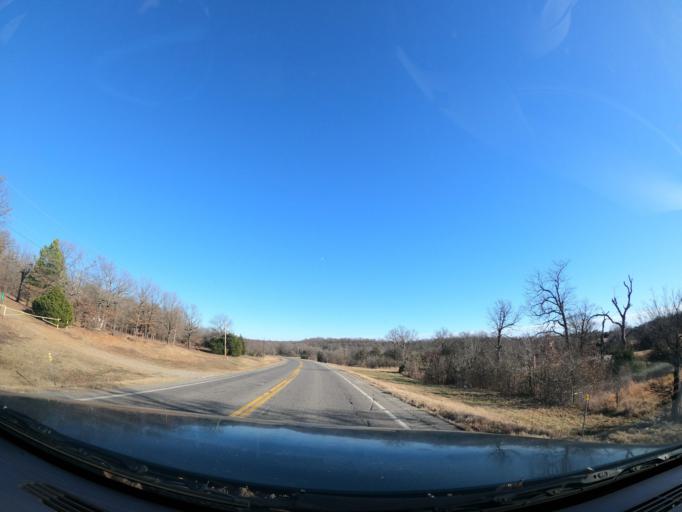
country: US
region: Oklahoma
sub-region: Pittsburg County
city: Longtown
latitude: 35.2146
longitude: -95.4203
